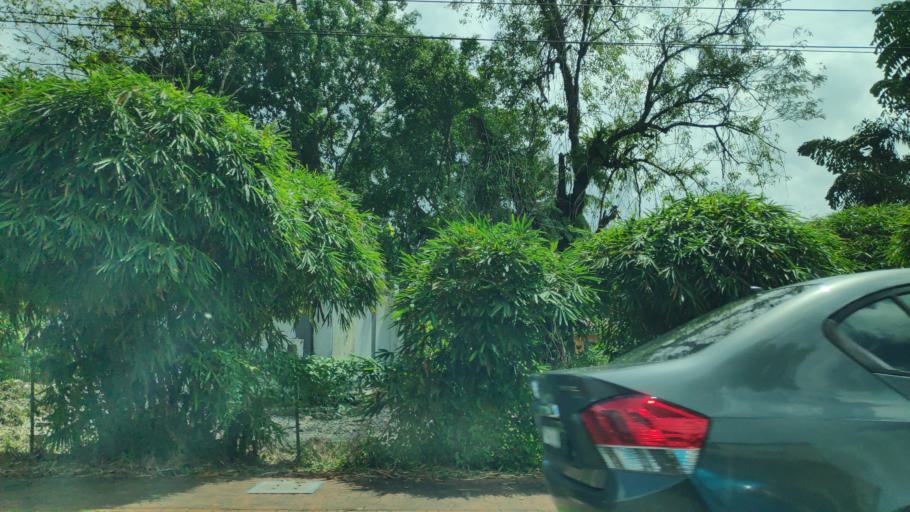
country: MY
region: Sarawak
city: Kuching
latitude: 1.5450
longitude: 110.3449
